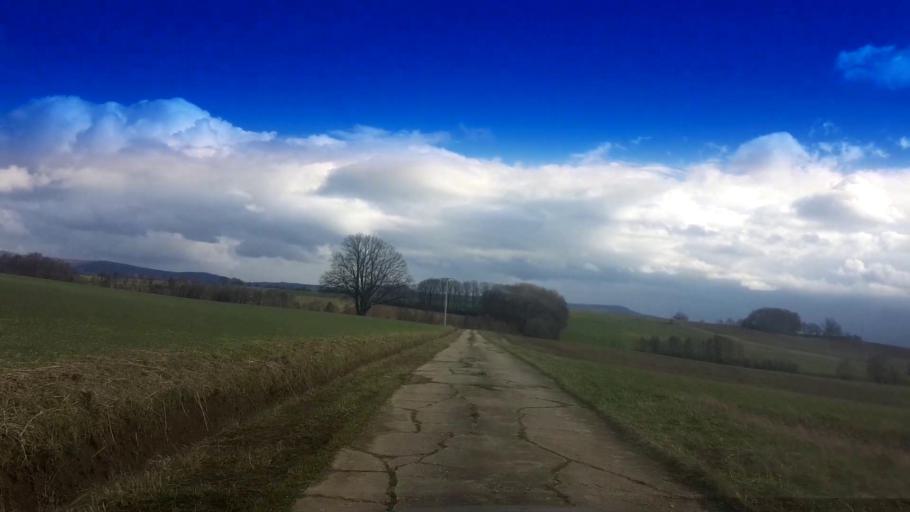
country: DE
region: Bavaria
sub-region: Upper Franconia
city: Schesslitz
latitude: 49.9926
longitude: 11.0170
